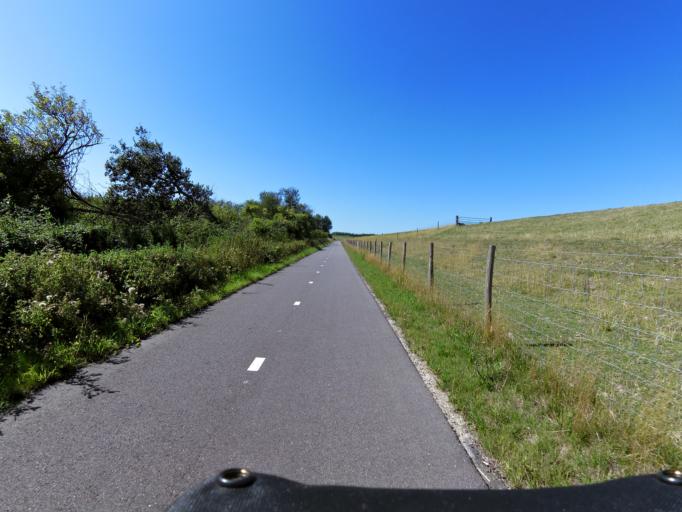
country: NL
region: South Holland
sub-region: Gemeente Goeree-Overflakkee
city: Goedereede
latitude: 51.8041
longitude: 3.9986
